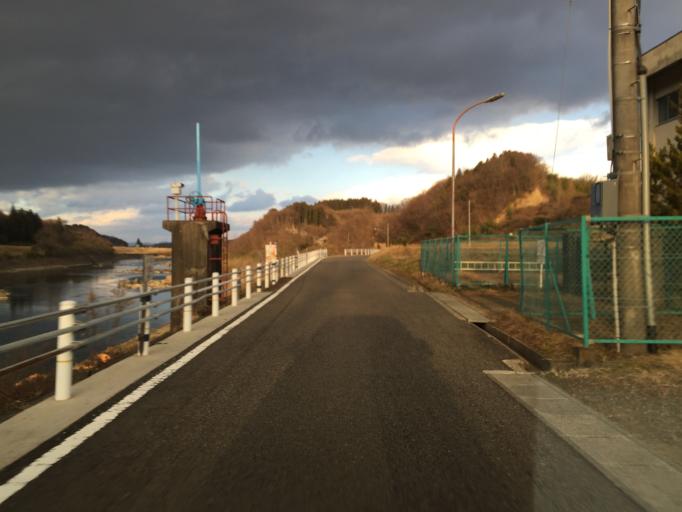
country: JP
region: Fukushima
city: Motomiya
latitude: 37.5427
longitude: 140.4245
